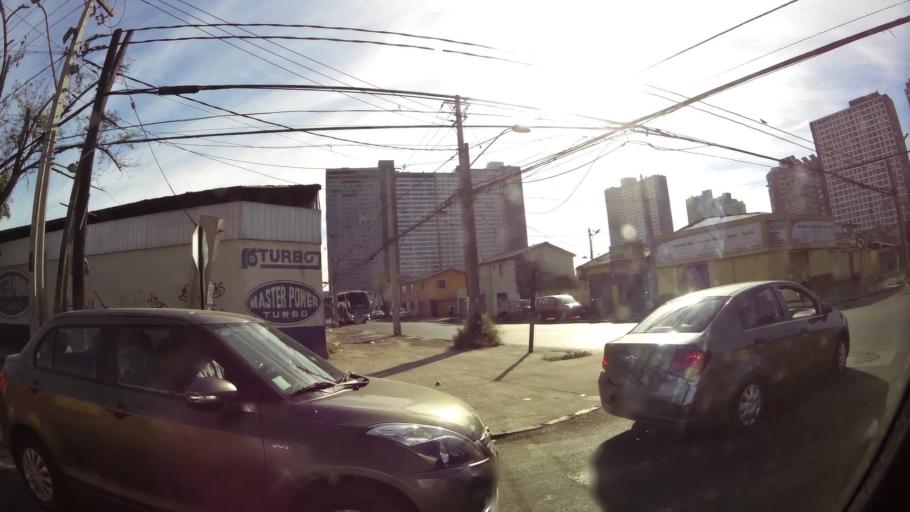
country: CL
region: Santiago Metropolitan
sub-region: Provincia de Santiago
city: Santiago
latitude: -33.4575
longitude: -70.6880
